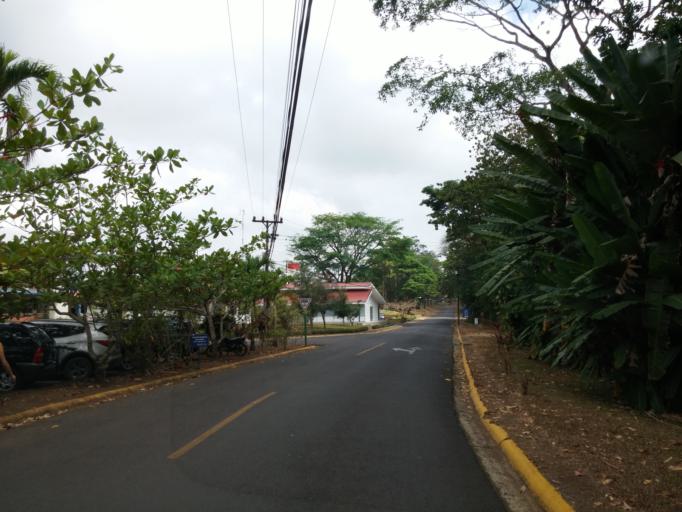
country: CR
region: Alajuela
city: Quesada
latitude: 10.3617
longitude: -84.5091
